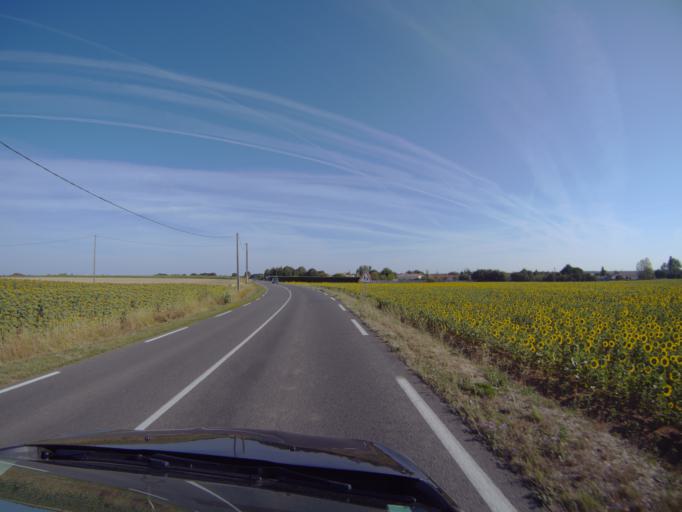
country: FR
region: Pays de la Loire
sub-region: Departement de la Vendee
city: Jard-sur-Mer
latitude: 46.4422
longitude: -1.5786
